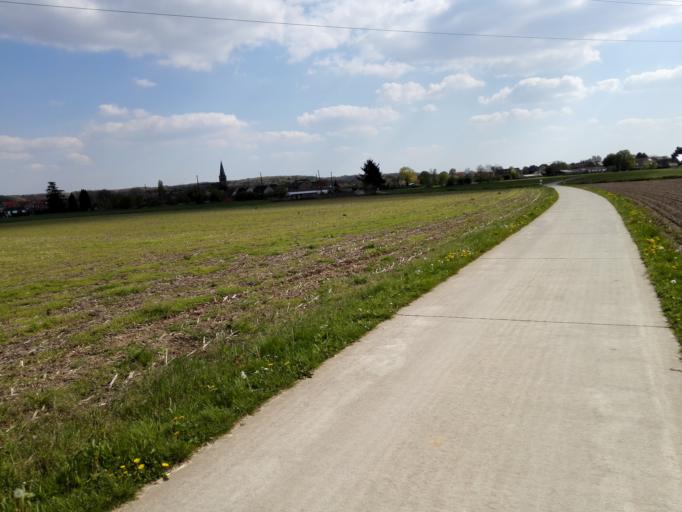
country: BE
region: Flanders
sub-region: Provincie Vlaams-Brabant
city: Rotselaar
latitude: 50.9334
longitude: 4.7207
